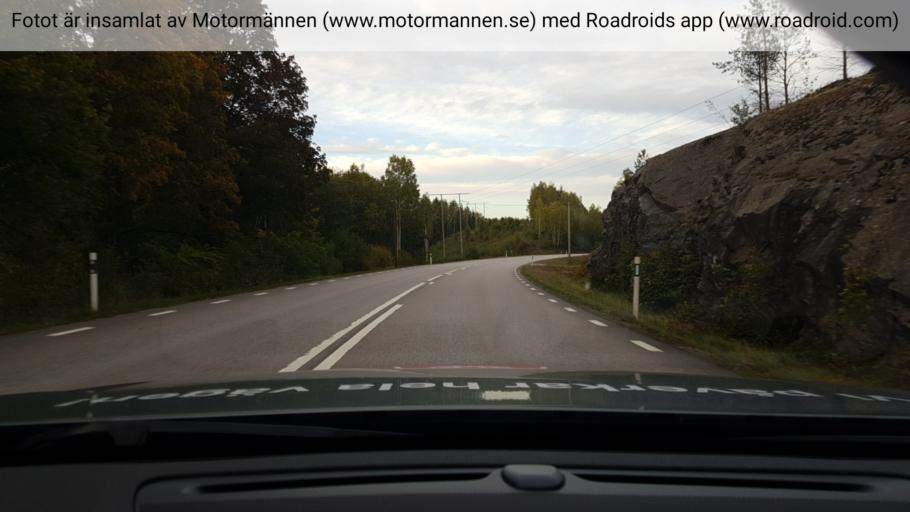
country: SE
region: Vaestra Goetaland
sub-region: Bengtsfors Kommun
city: Bengtsfors
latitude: 59.0199
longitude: 12.2708
